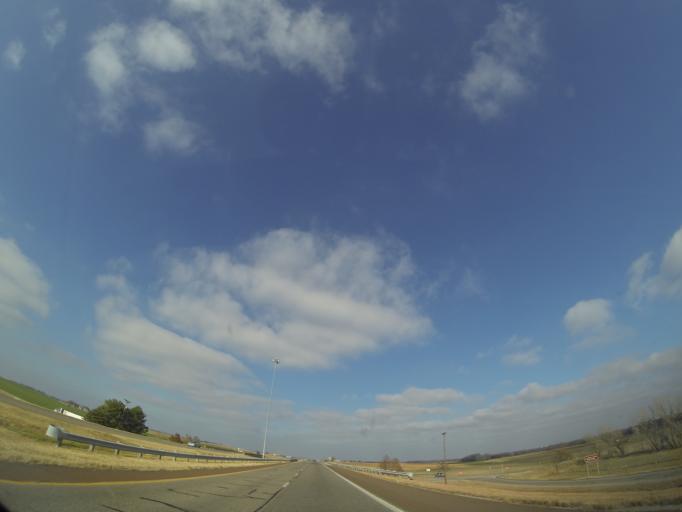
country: US
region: Kansas
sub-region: McPherson County
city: Lindsborg
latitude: 38.5498
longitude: -97.6207
